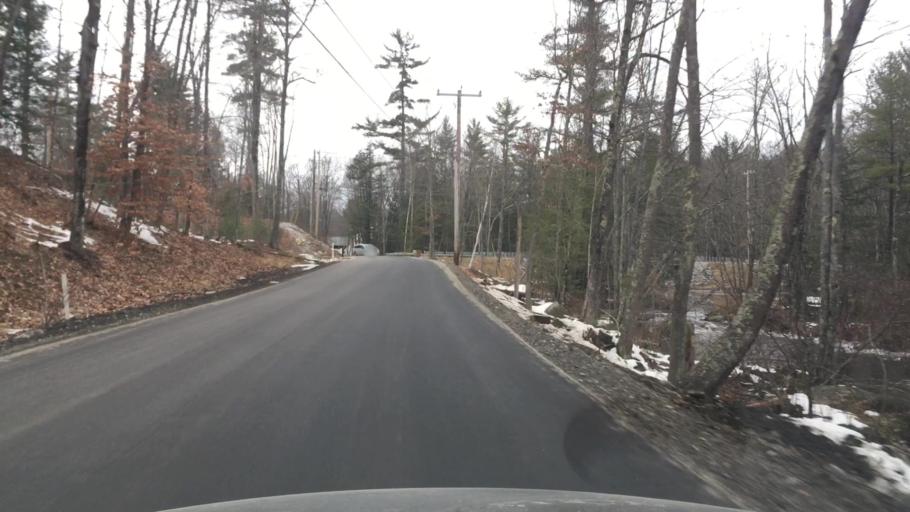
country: US
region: New Hampshire
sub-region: Hillsborough County
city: New Boston
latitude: 43.0046
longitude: -71.6641
